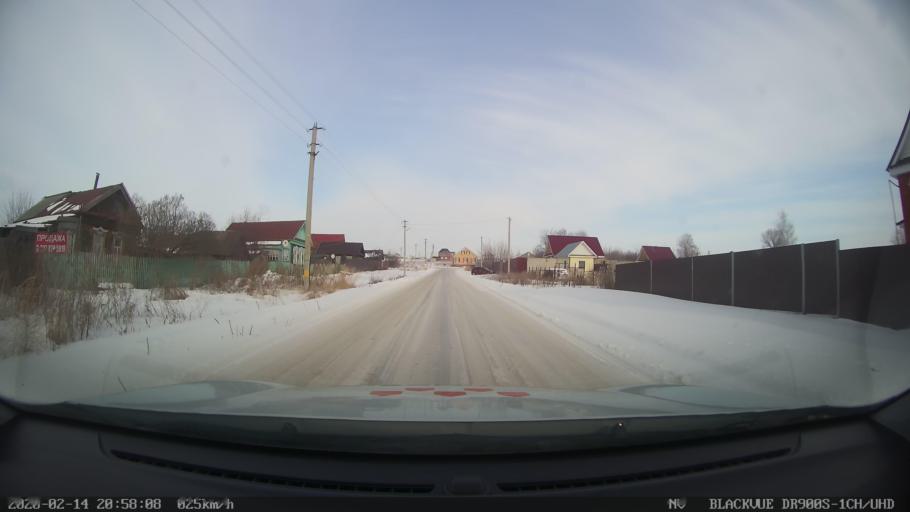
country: RU
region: Tatarstan
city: Kuybyshevskiy Zaton
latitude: 55.1775
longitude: 49.2477
